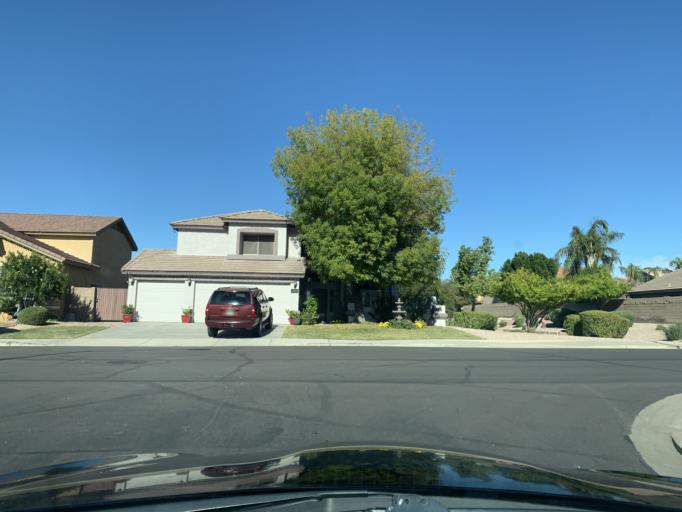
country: US
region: Arizona
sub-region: Pinal County
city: Apache Junction
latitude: 33.3825
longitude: -111.6223
